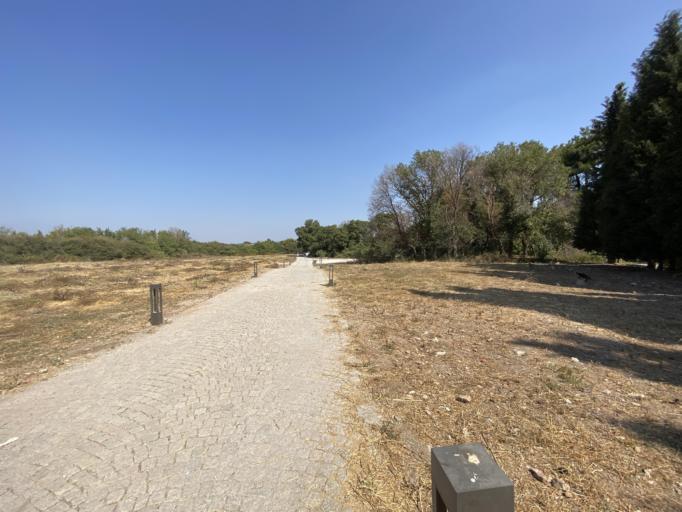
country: TR
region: Izmir
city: Selcuk
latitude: 37.9429
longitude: 27.3406
